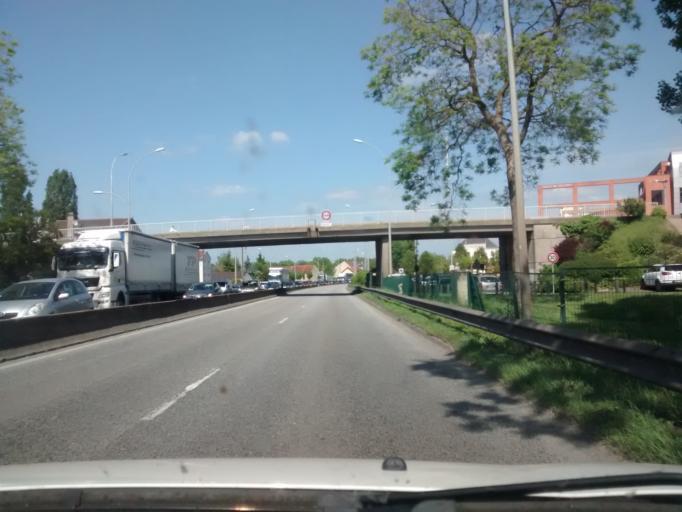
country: FR
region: Ile-de-France
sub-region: Departement des Yvelines
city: Trappes
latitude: 48.7759
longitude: 1.9978
